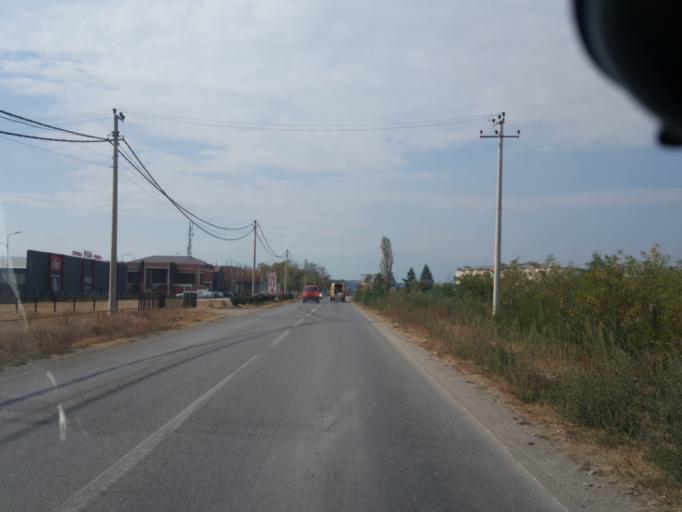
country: XK
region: Gjakova
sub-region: Komuna e Gjakoves
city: Gjakove
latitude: 42.3712
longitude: 20.4528
